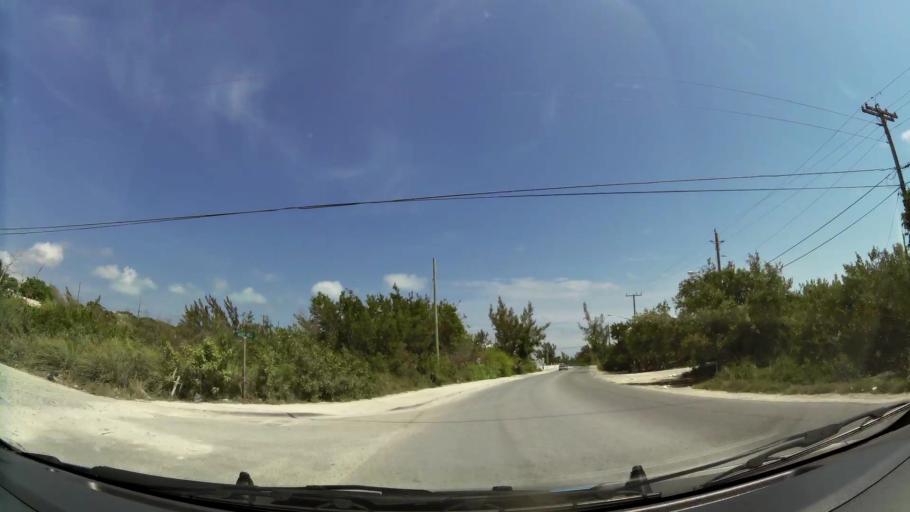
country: BS
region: Mayaguana
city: Abraham's Bay
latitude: 21.7602
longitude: -72.2637
